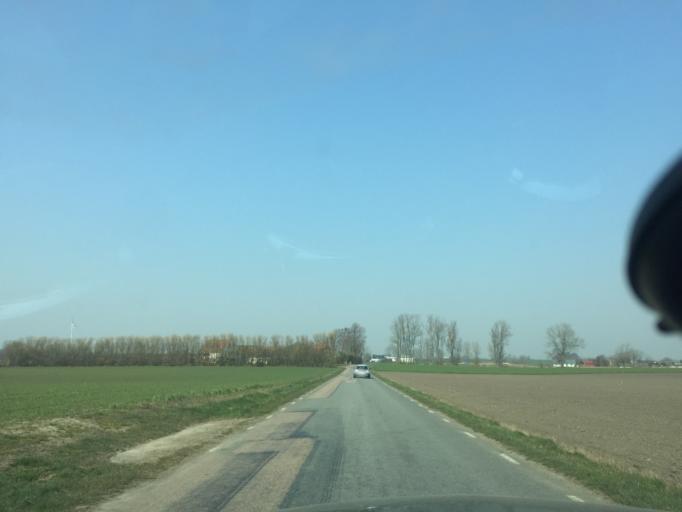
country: SE
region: Skane
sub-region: Simrishamns Kommun
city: Simrishamn
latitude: 55.4631
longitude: 14.2096
